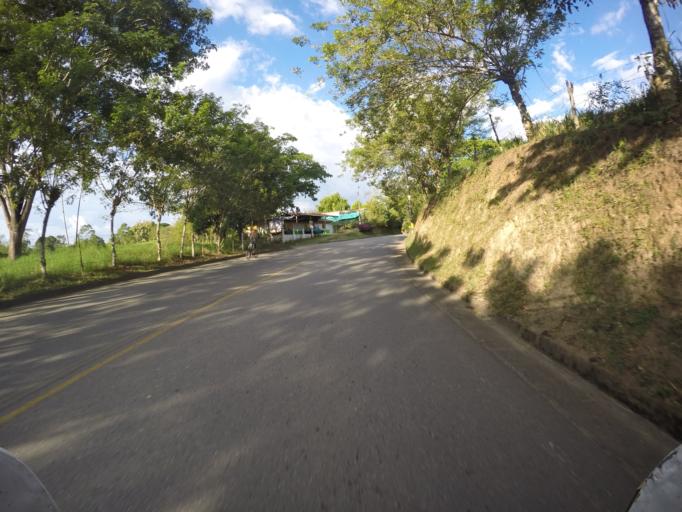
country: CO
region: Valle del Cauca
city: Alcala
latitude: 4.6819
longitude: -75.8022
